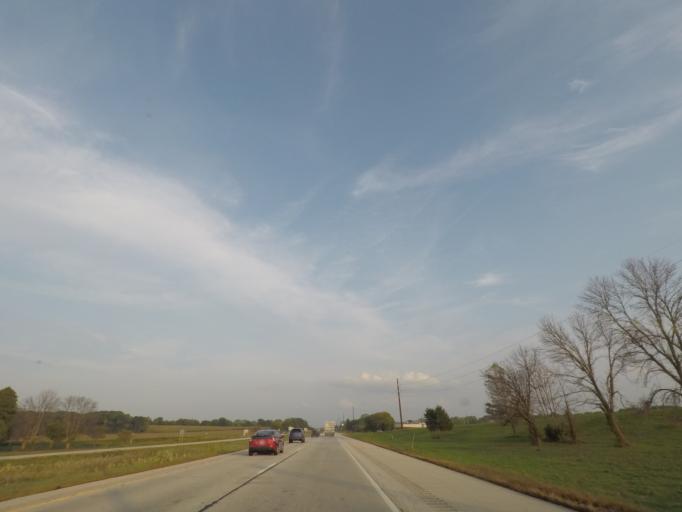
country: US
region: Wisconsin
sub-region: Jefferson County
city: Lake Mills
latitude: 43.0929
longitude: -88.9084
